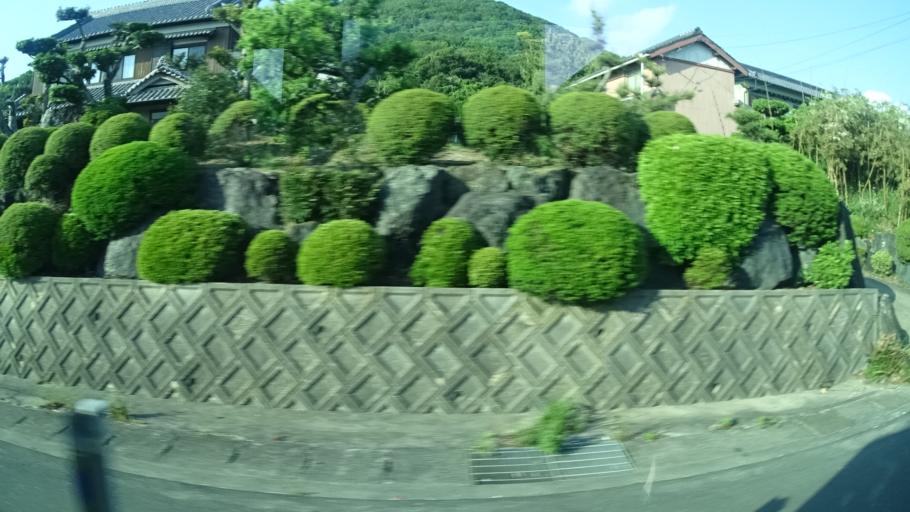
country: JP
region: Aichi
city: Tahara
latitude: 34.6502
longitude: 137.2212
